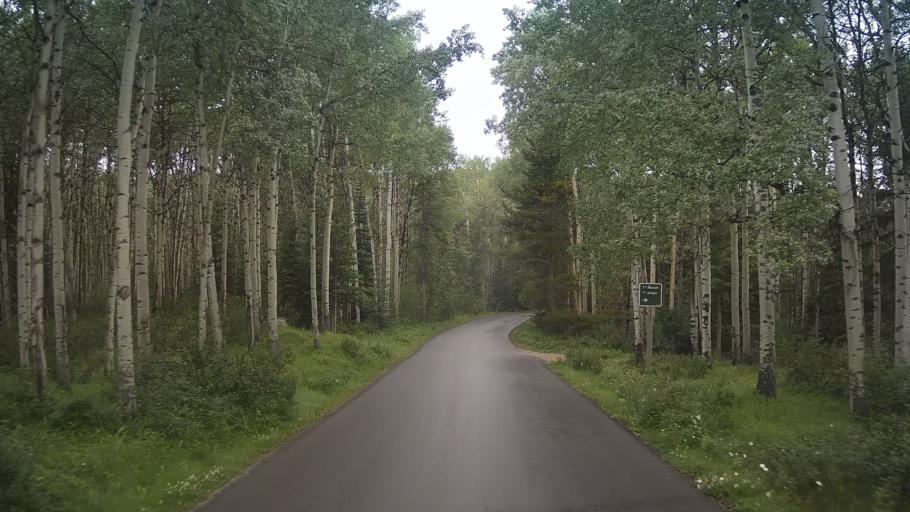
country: CA
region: Alberta
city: Jasper Park Lodge
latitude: 52.9136
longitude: -118.0940
